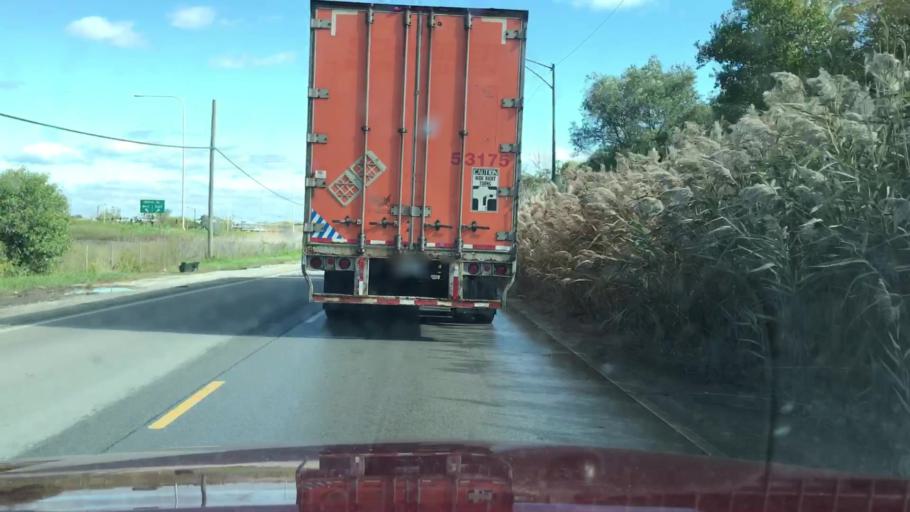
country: US
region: Illinois
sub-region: Cook County
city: Dolton
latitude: 41.7054
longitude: -87.5872
